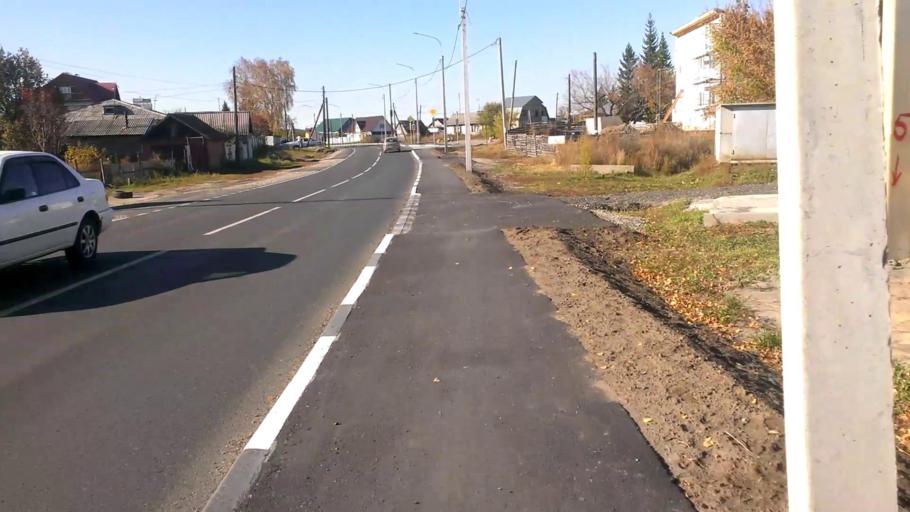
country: RU
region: Altai Krai
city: Sannikovo
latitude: 53.3154
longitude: 83.9596
